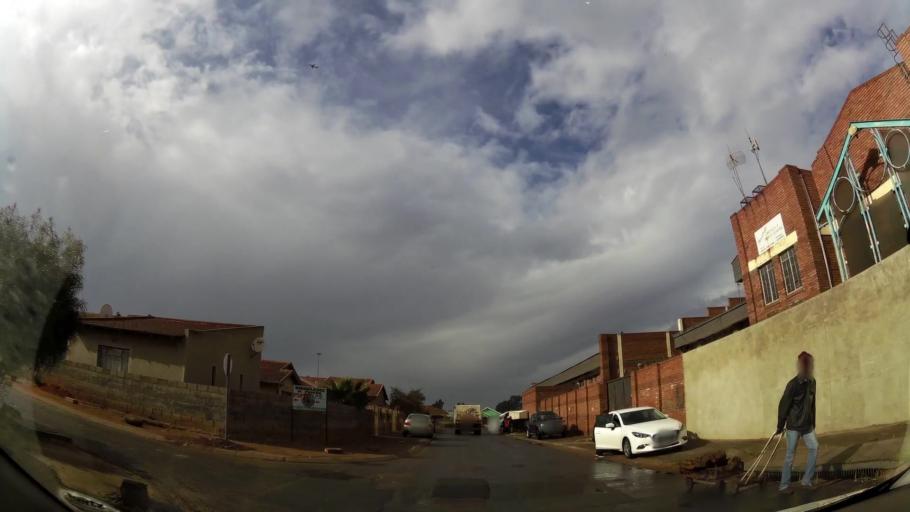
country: ZA
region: Gauteng
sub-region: Ekurhuleni Metropolitan Municipality
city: Germiston
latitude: -26.3268
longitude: 28.1862
